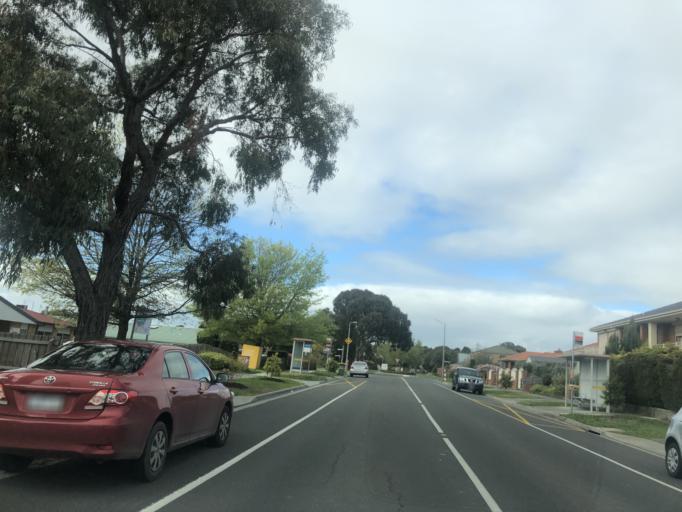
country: AU
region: Victoria
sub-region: Knox
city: Rowville
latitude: -37.9328
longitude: 145.2413
